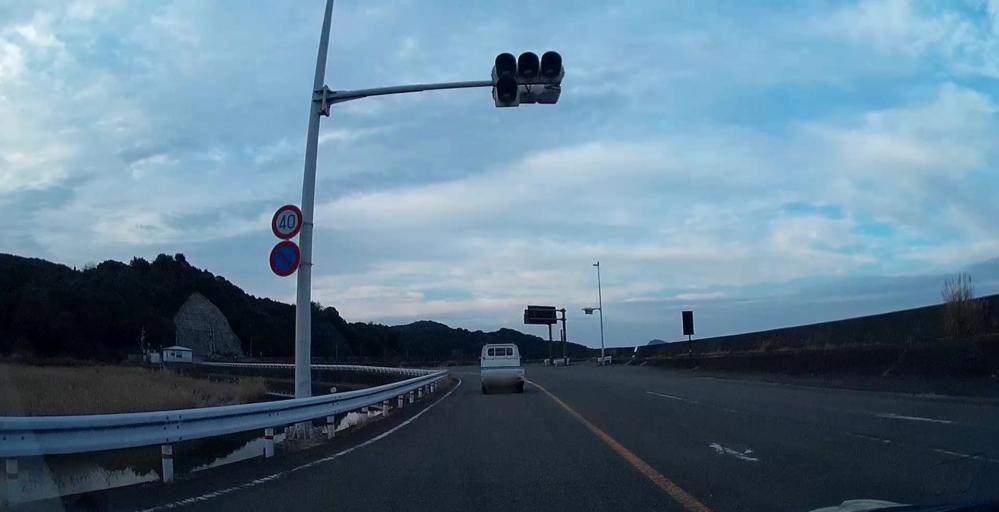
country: JP
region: Kumamoto
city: Hondo
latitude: 32.4996
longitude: 130.3928
